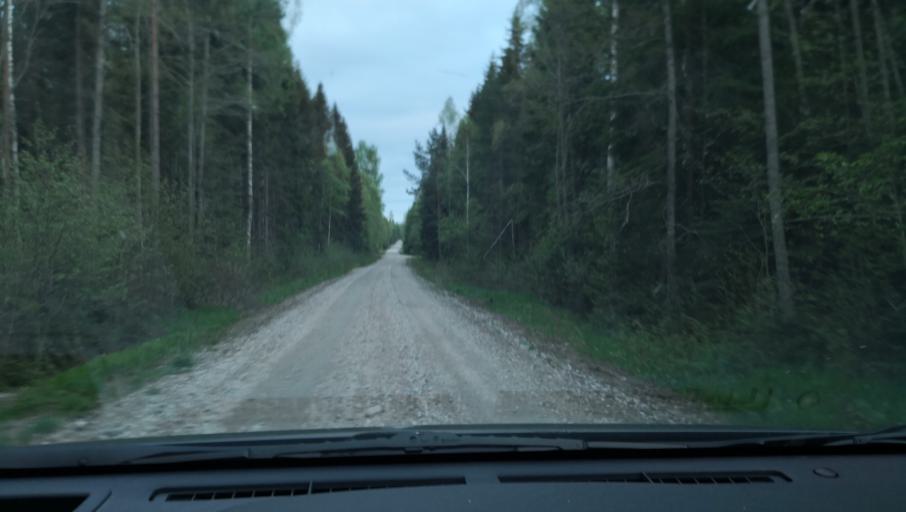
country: SE
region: Vaestmanland
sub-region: Skinnskattebergs Kommun
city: Skinnskatteberg
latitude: 59.7707
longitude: 15.4546
